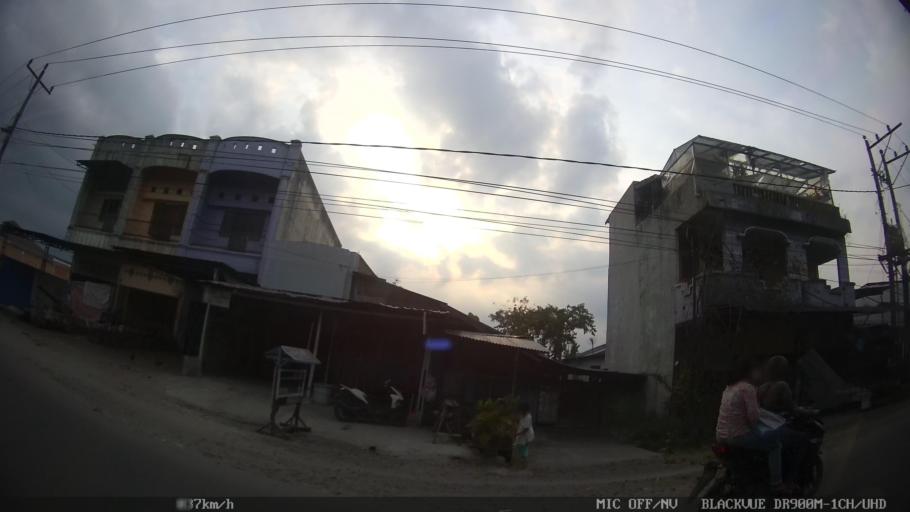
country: ID
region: North Sumatra
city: Sunggal
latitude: 3.5703
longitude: 98.6101
